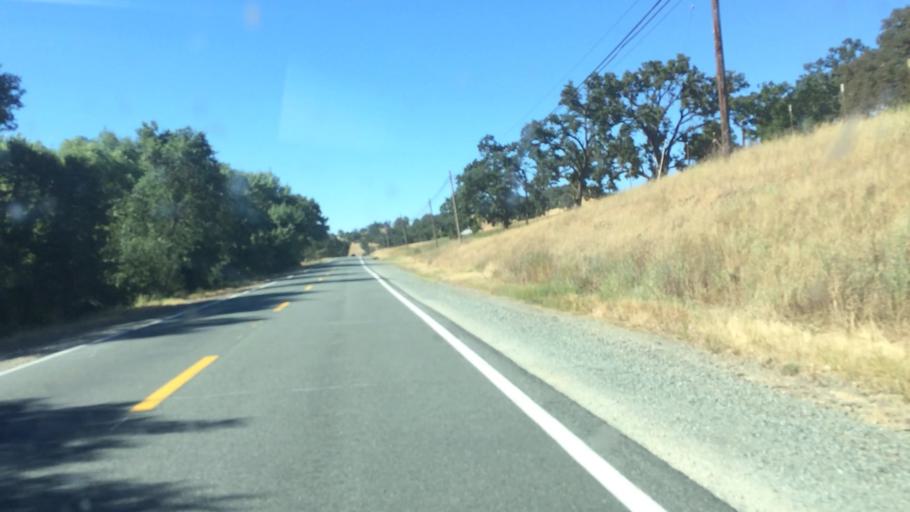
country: US
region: California
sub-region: Amador County
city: Plymouth
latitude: 38.4993
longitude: -120.8480
